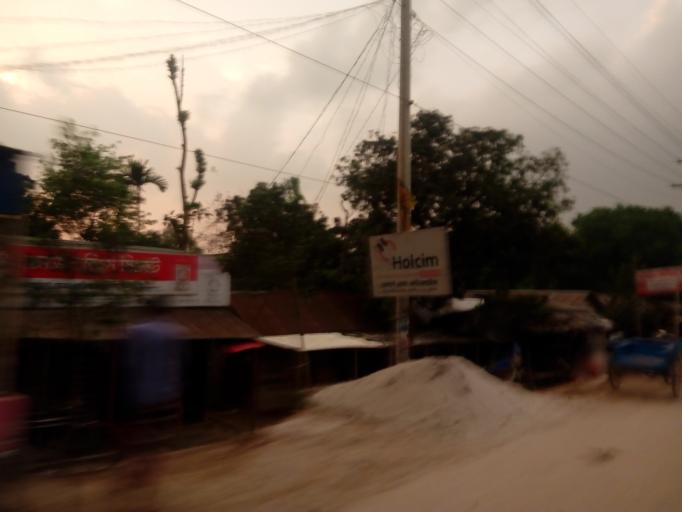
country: BD
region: Rajshahi
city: Shahzadpur
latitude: 24.2988
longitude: 89.6972
